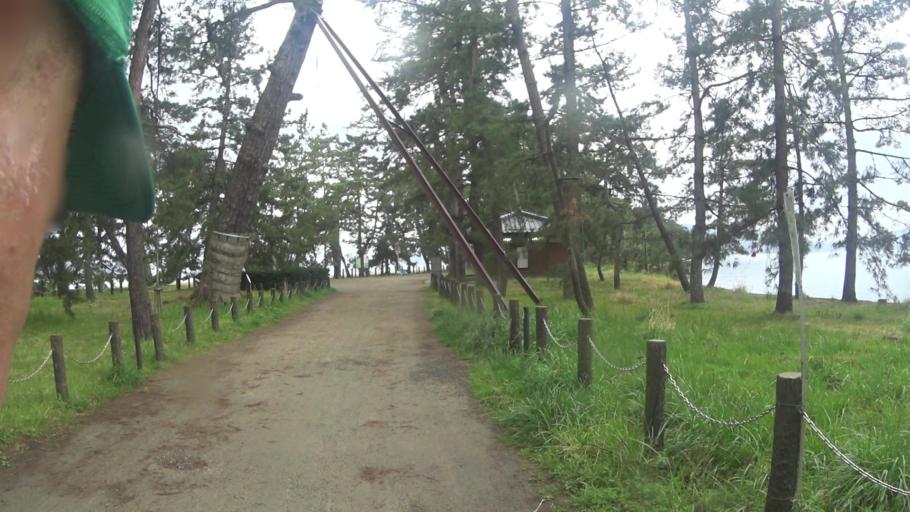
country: JP
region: Kyoto
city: Miyazu
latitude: 35.5778
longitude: 135.1979
